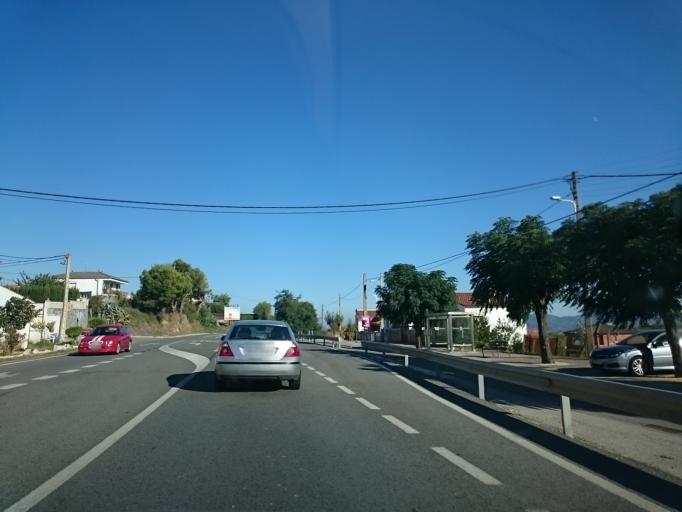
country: ES
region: Catalonia
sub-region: Provincia de Barcelona
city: Piera
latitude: 41.5056
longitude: 1.7786
